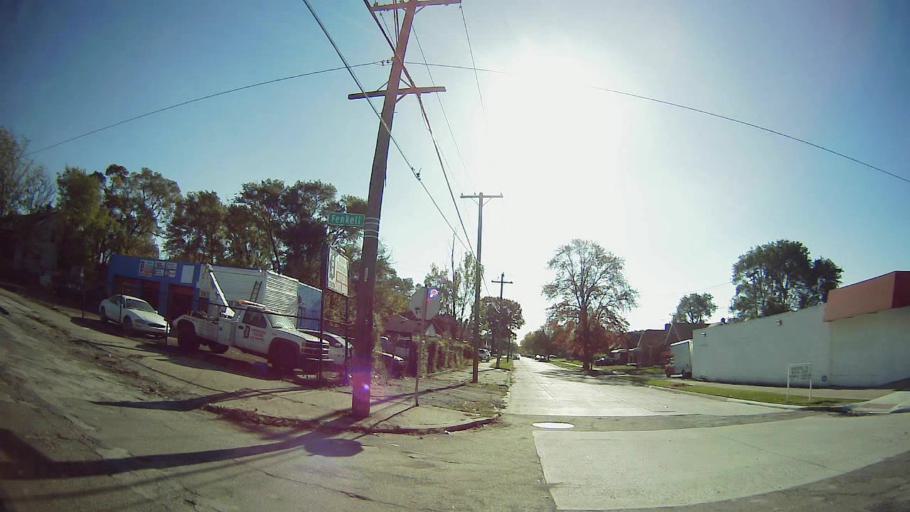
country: US
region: Michigan
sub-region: Oakland County
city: Oak Park
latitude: 42.4021
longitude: -83.1781
